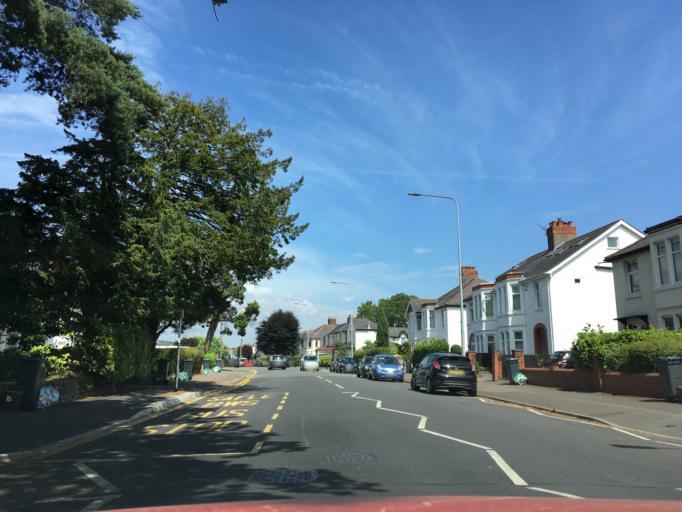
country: GB
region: Wales
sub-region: Cardiff
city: Cardiff
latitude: 51.5109
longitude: -3.1823
